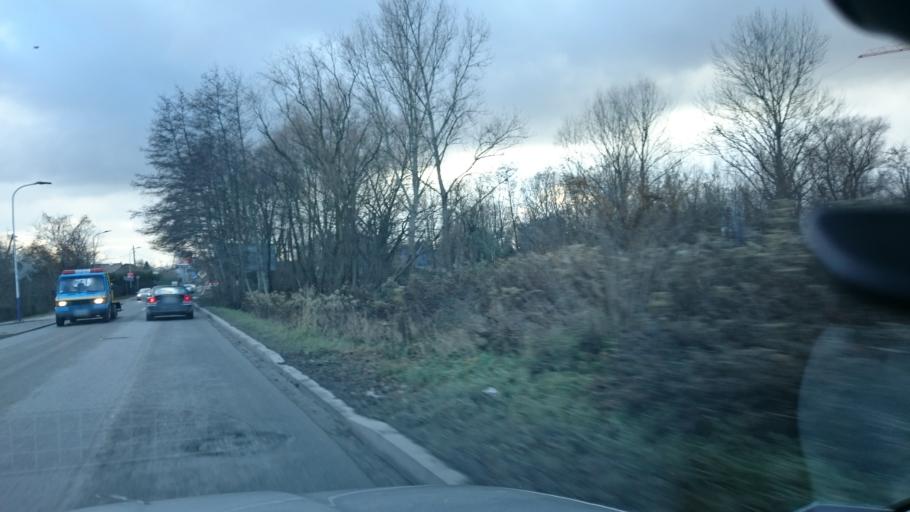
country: PL
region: Lesser Poland Voivodeship
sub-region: Powiat wielicki
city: Czarnochowice
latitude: 50.0161
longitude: 20.0282
